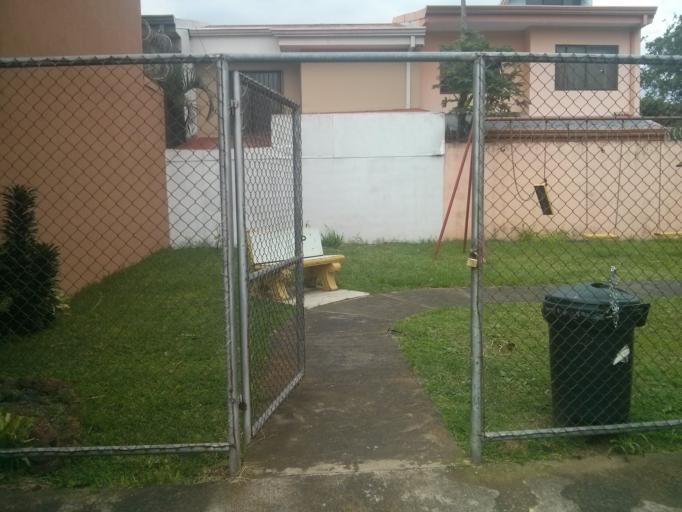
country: CR
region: San Jose
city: Curridabat
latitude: 9.9019
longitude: -84.0531
